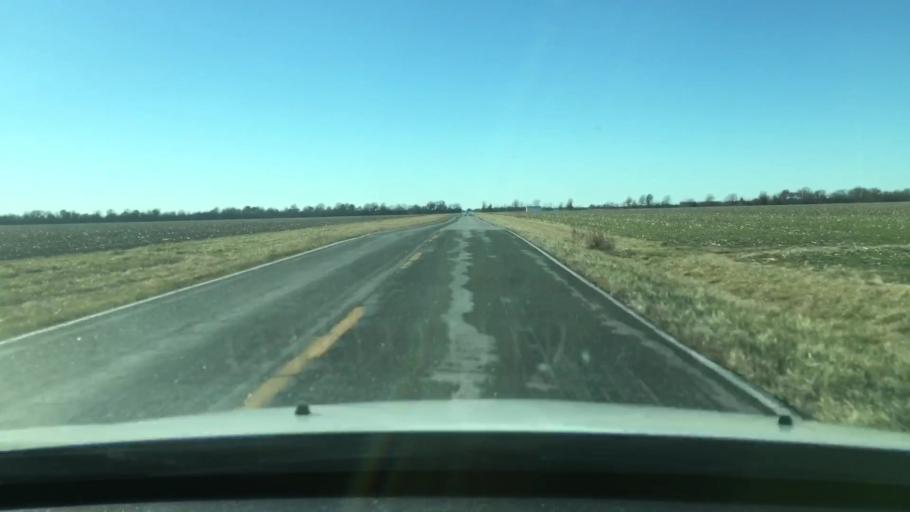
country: US
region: Missouri
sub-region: Audrain County
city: Vandalia
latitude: 39.2813
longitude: -91.6742
